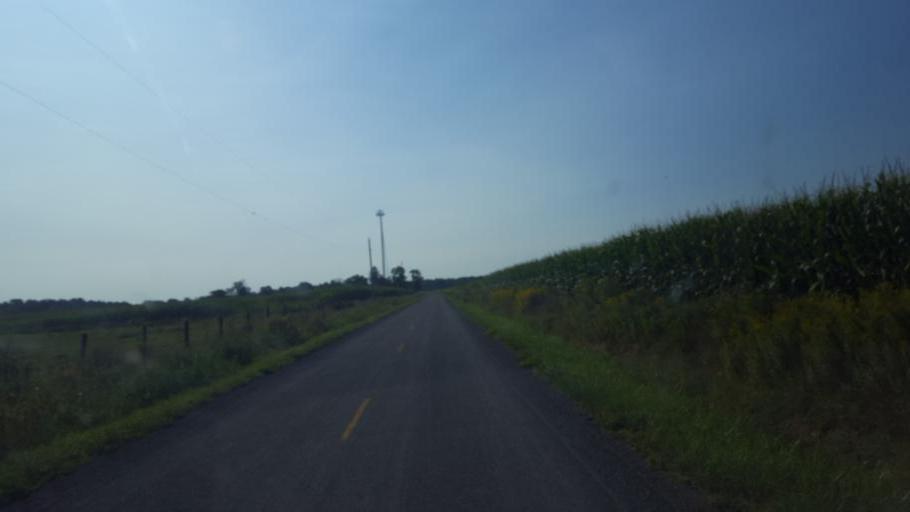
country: US
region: Ohio
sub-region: Ashtabula County
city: Orwell
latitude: 41.4741
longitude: -80.8852
